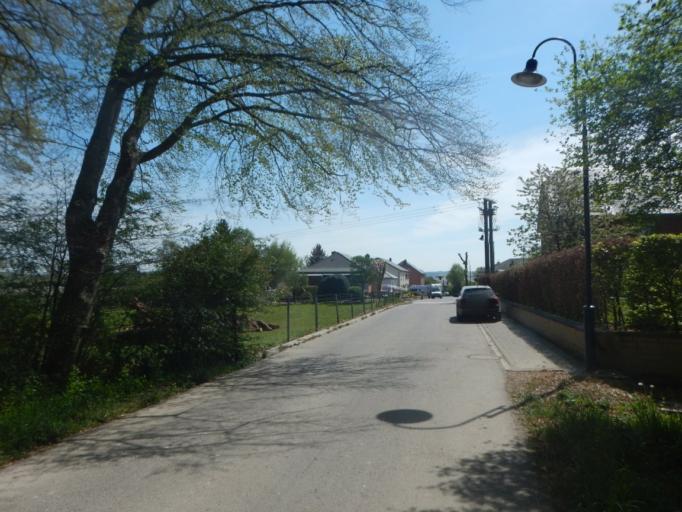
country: LU
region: Diekirch
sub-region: Canton de Redange
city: Redange-sur-Attert
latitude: 49.7572
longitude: 5.9093
